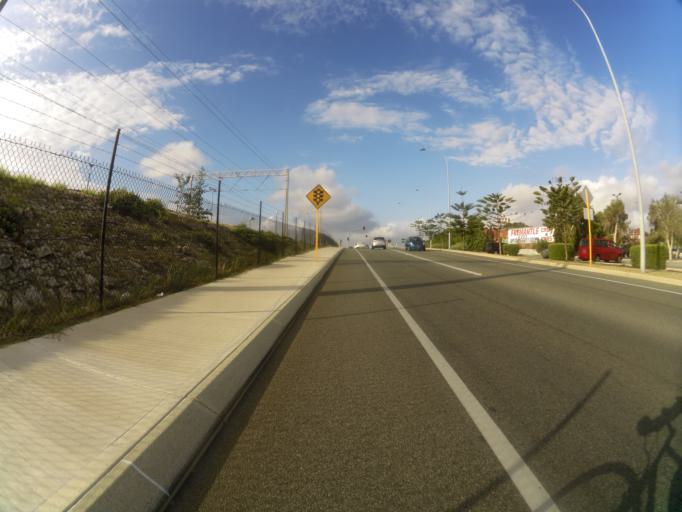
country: AU
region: Western Australia
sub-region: Fremantle
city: North Fremantle
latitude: -32.0447
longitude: 115.7522
